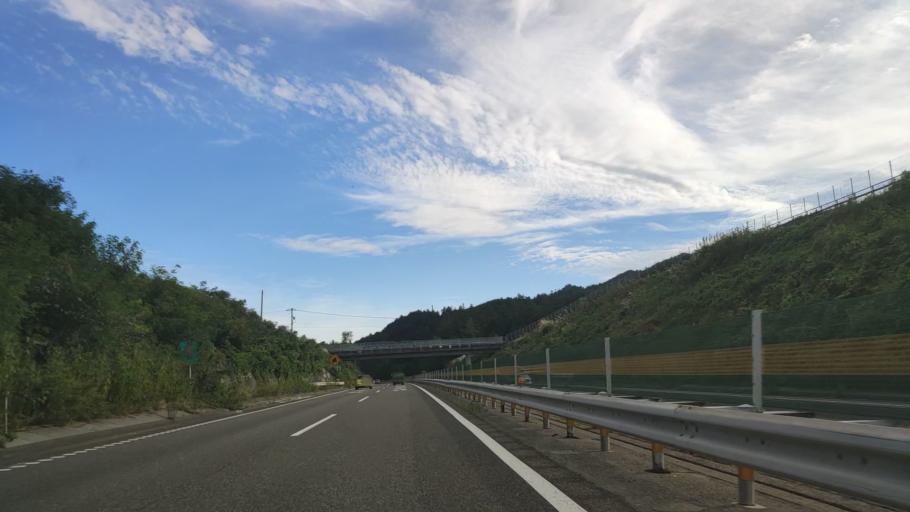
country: JP
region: Nagano
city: Ina
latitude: 35.8028
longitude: 137.9293
